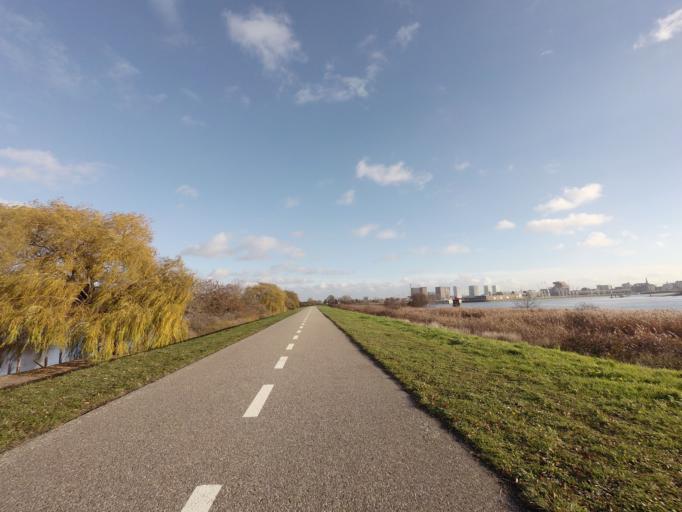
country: BE
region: Flanders
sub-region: Provincie Antwerpen
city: Antwerpen
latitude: 51.2402
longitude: 4.3918
